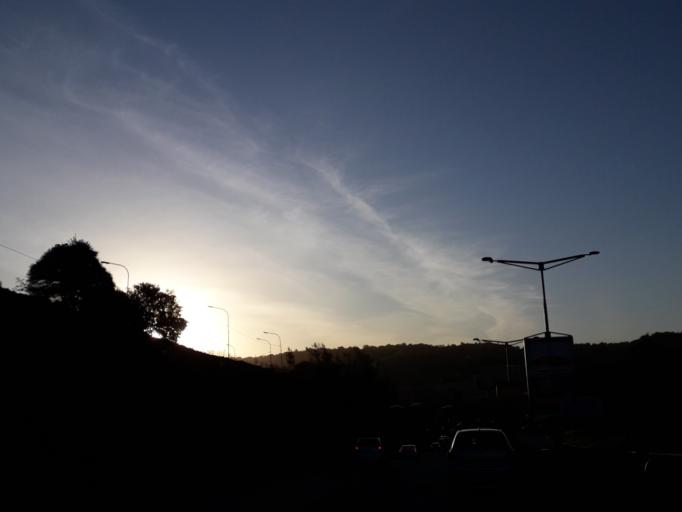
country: ZA
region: Gauteng
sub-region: City of Johannesburg Metropolitan Municipality
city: Roodepoort
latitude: -26.1519
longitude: 27.9304
